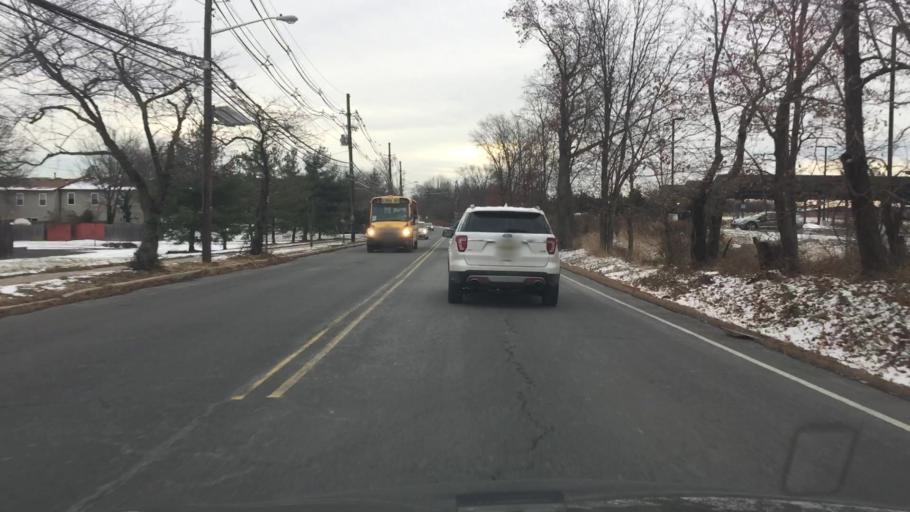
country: US
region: New Jersey
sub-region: Middlesex County
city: Society Hill
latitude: 40.5293
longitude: -74.4374
